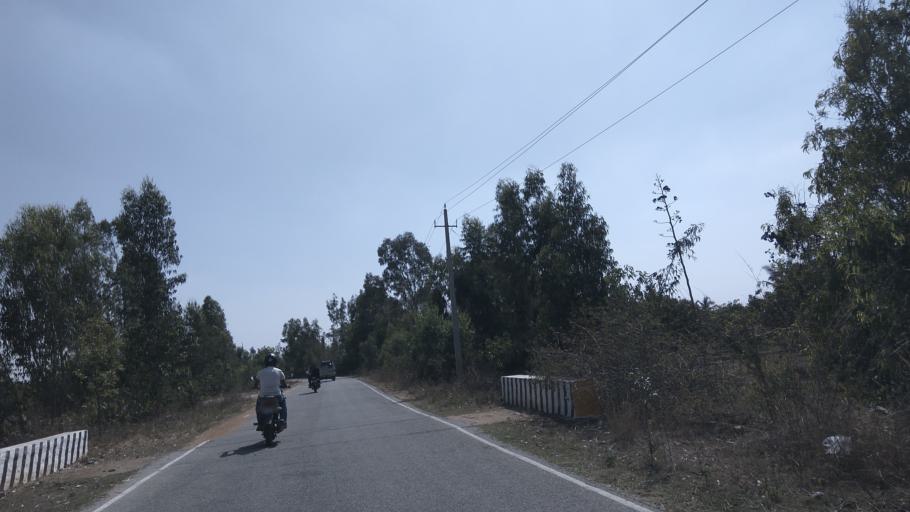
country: IN
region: Karnataka
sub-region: Kolar
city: Mulbagal
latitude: 13.1923
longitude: 78.3542
